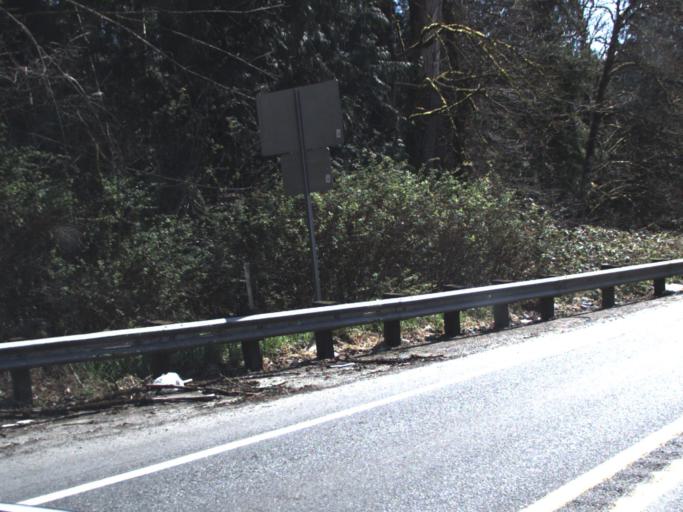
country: US
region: Washington
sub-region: King County
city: Black Diamond
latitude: 47.2783
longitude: -121.9908
